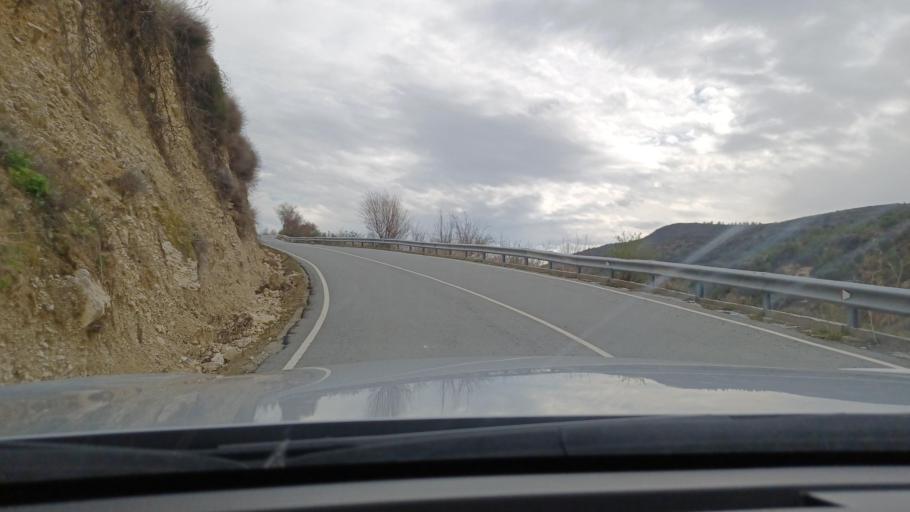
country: CY
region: Limassol
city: Pelendri
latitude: 34.8117
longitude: 32.9062
